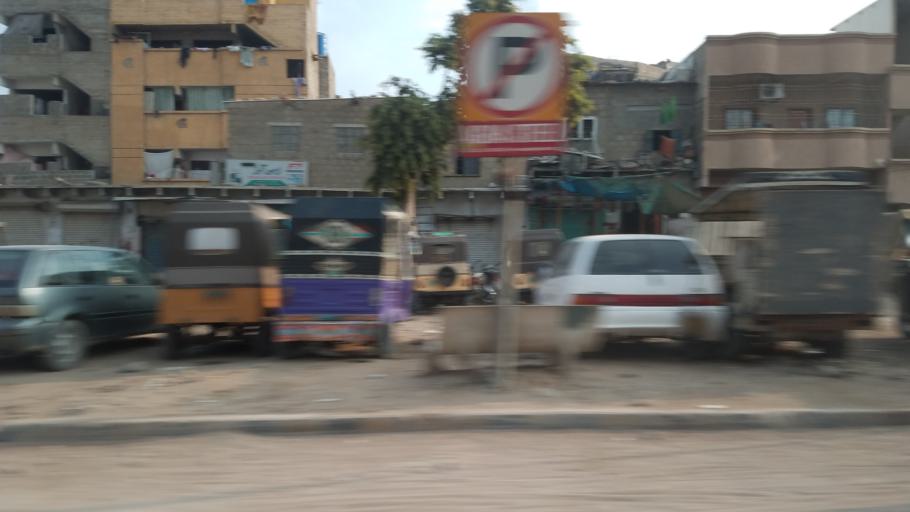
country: PK
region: Sindh
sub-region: Karachi District
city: Karachi
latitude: 24.9283
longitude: 67.0883
